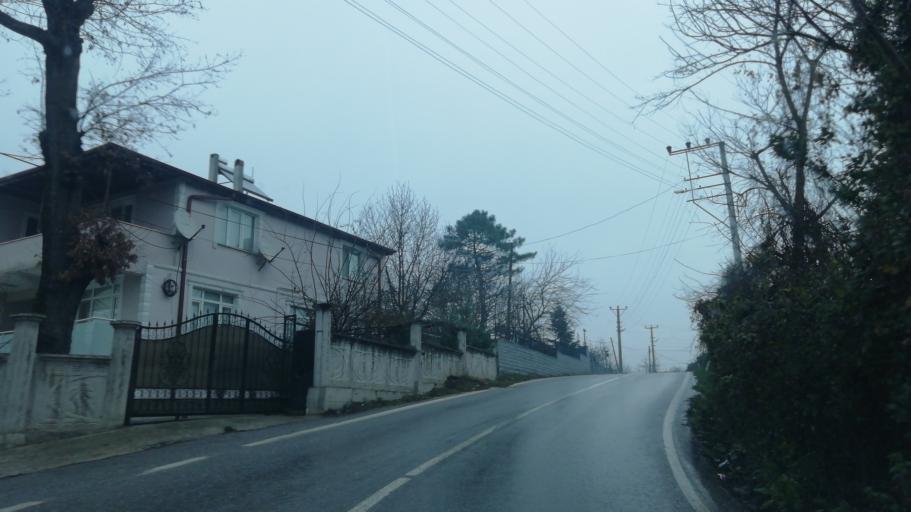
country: TR
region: Sakarya
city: Karapurcek
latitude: 40.6826
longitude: 30.5245
